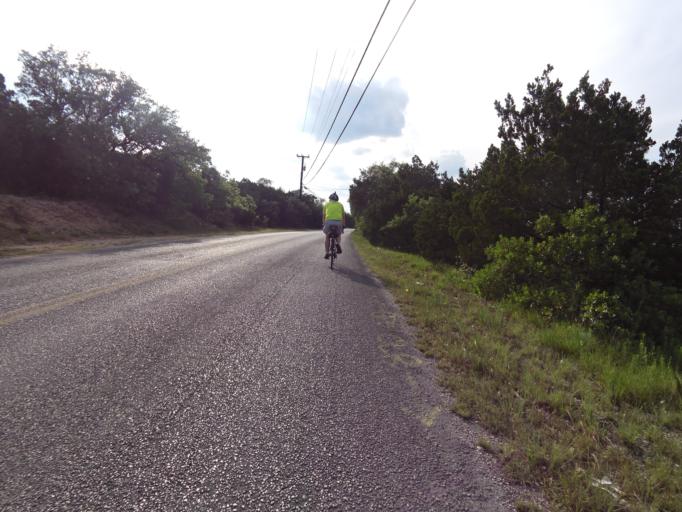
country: US
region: Texas
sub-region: Bexar County
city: Cross Mountain
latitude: 29.6615
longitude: -98.6317
